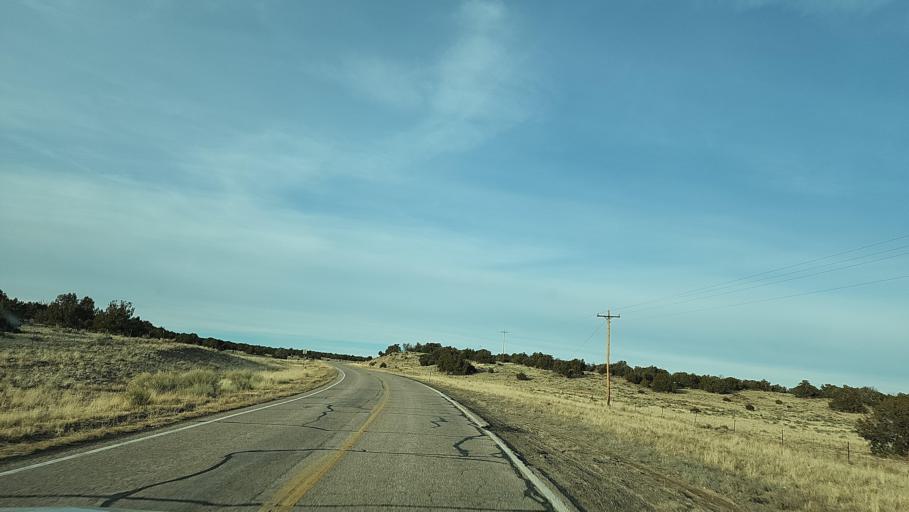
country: US
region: New Mexico
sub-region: Catron County
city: Reserve
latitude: 34.4058
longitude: -108.4373
